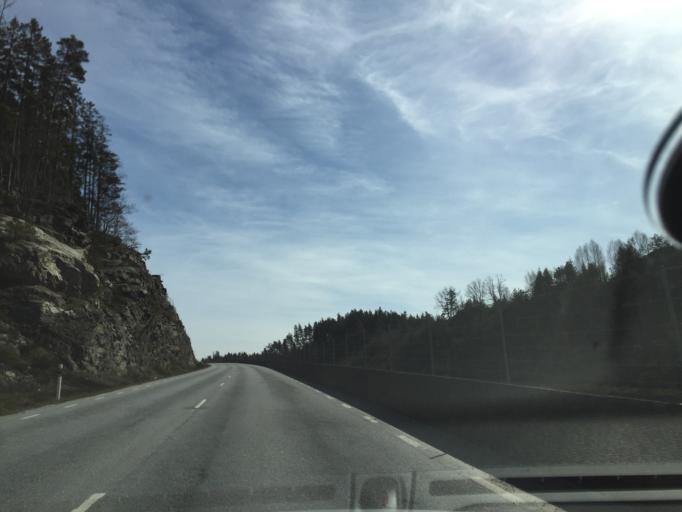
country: SE
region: Vaestra Goetaland
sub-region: Uddevalla Kommun
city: Uddevalla
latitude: 58.3681
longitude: 11.7953
